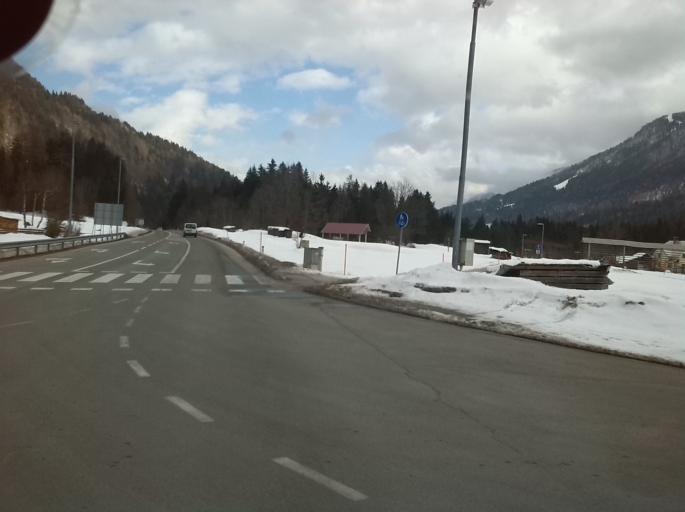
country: AT
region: Carinthia
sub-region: Politischer Bezirk Villach Land
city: Arnoldstein
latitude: 46.4943
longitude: 13.7209
